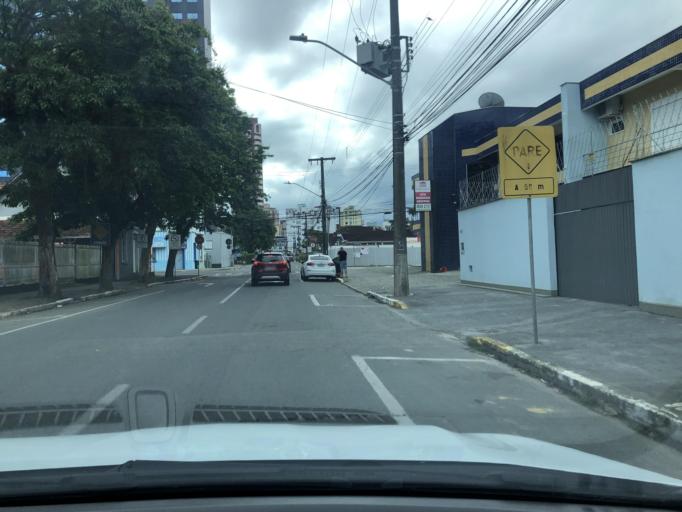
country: BR
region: Santa Catarina
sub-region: Joinville
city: Joinville
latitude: -26.3044
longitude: -48.8414
